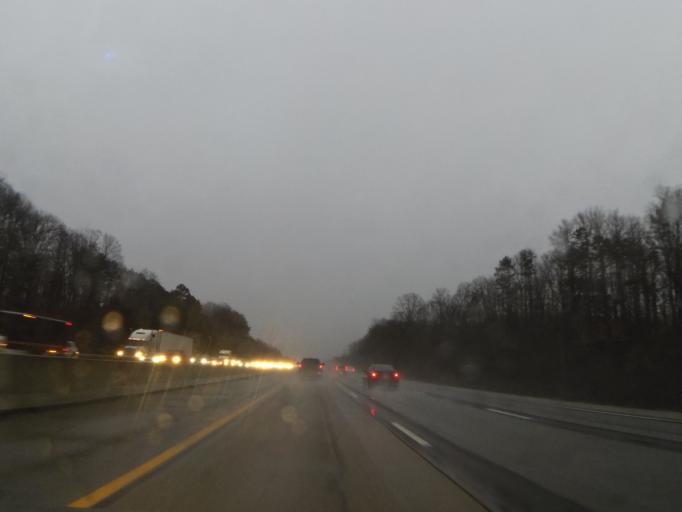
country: US
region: Kentucky
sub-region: Rockcastle County
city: Mount Vernon
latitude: 37.2925
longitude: -84.2715
